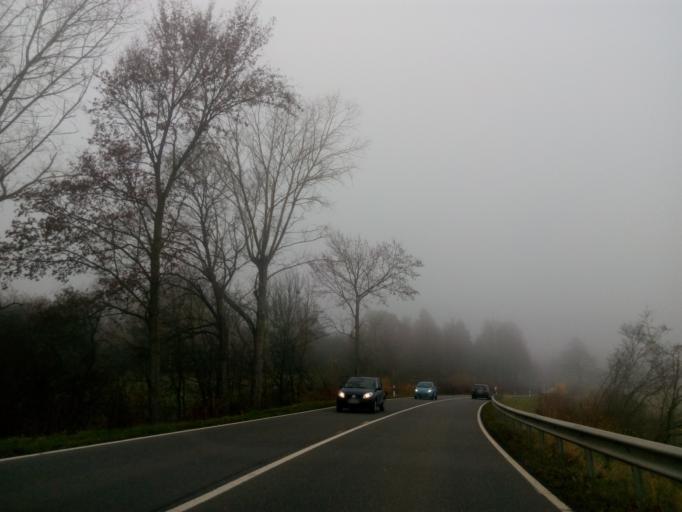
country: DE
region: Rheinland-Pfalz
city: Sien
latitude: 49.6919
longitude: 7.5092
